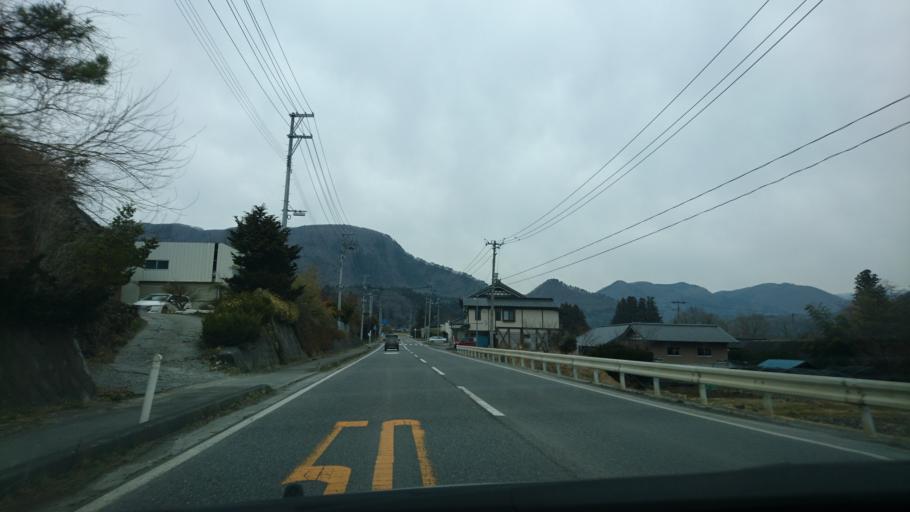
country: JP
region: Iwate
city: Tono
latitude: 39.1903
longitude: 141.5628
